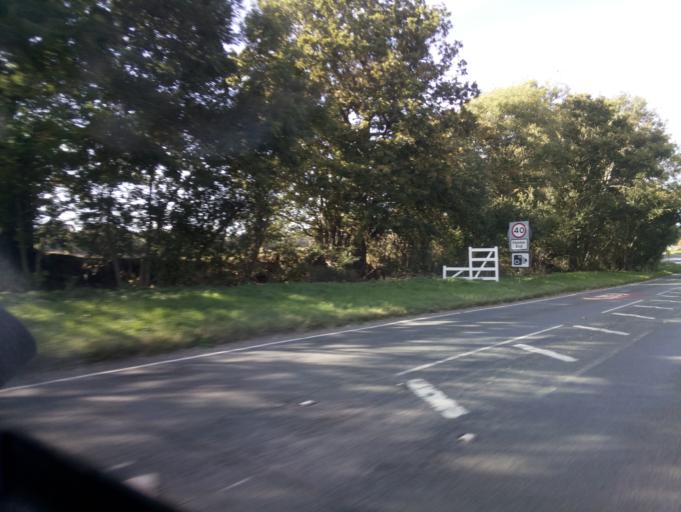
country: GB
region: England
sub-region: Hampshire
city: Tadley
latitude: 51.3192
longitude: -1.1213
